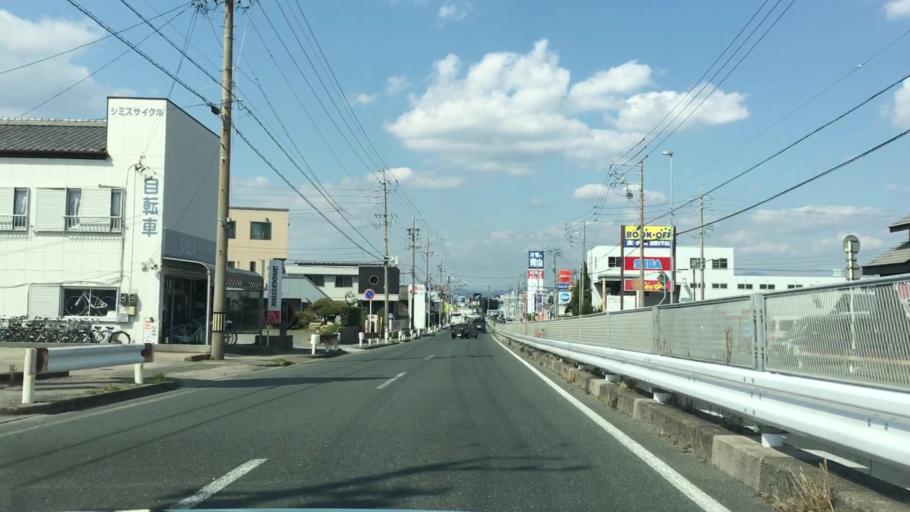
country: JP
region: Aichi
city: Toyohashi
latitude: 34.7487
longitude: 137.4134
